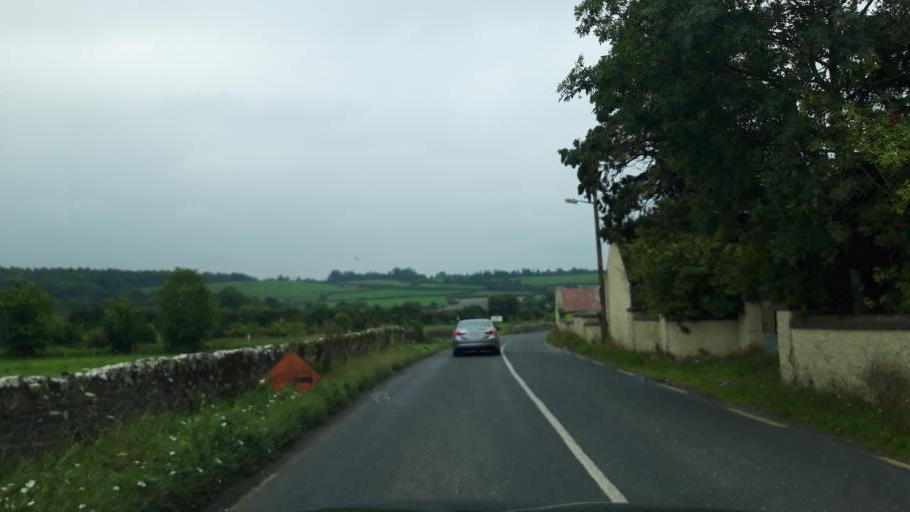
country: IE
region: Munster
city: Fethard
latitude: 52.4617
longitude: -7.7026
